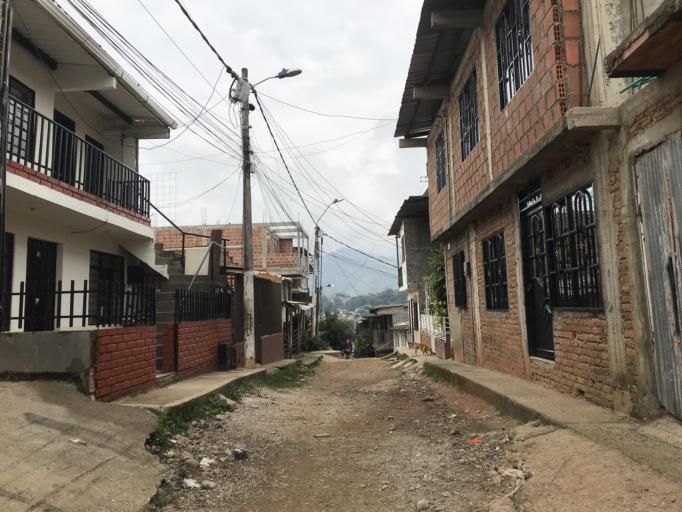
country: CO
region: Valle del Cauca
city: Cali
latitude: 3.3741
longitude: -76.5591
